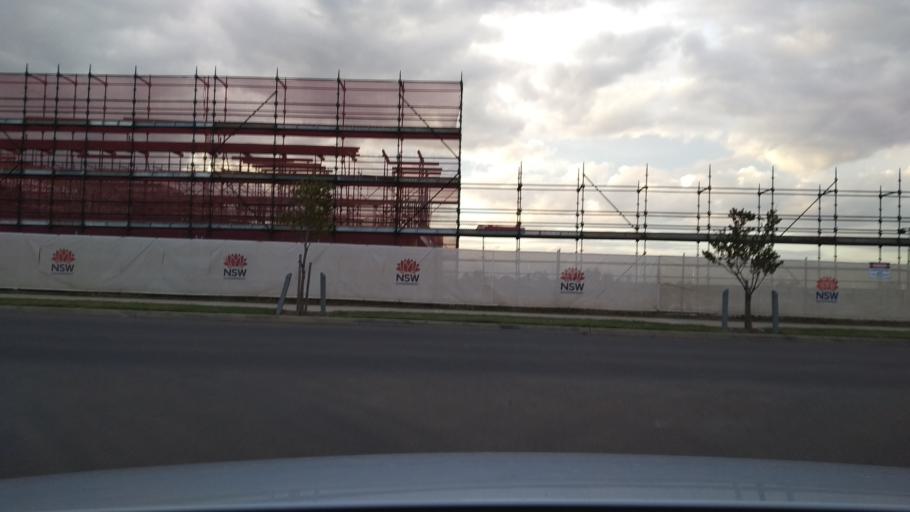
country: AU
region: New South Wales
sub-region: Camden
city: Narellan
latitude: -33.9992
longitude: 150.7366
